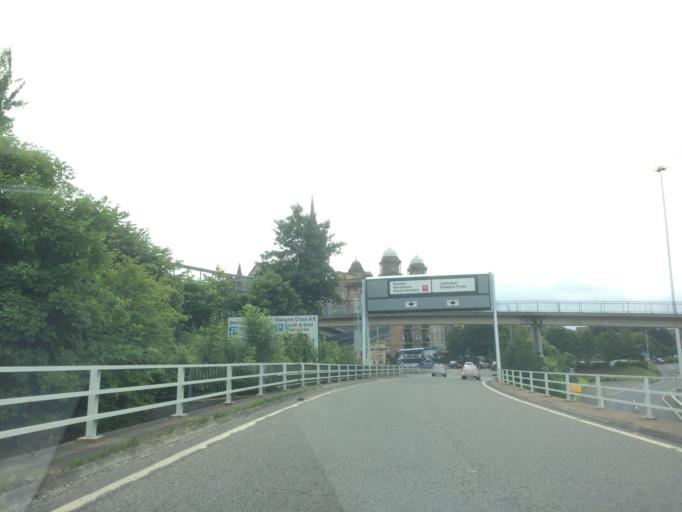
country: GB
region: Scotland
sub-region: Glasgow City
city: Glasgow
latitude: 55.8661
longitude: -4.2362
